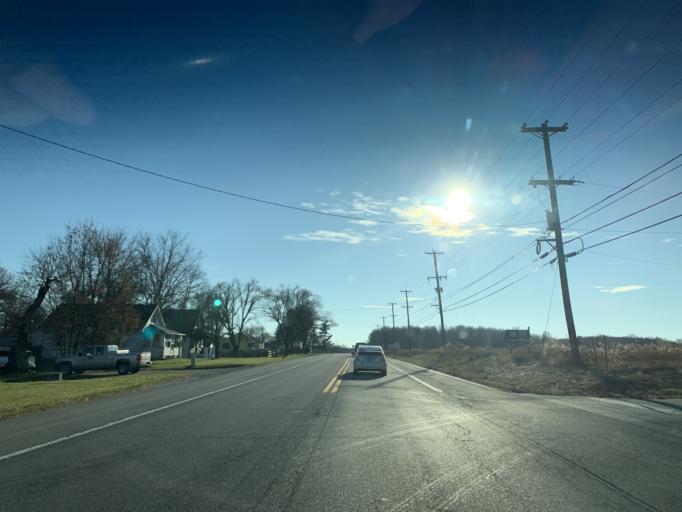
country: US
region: Maryland
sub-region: Cecil County
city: Elkton
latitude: 39.5033
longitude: -75.8345
